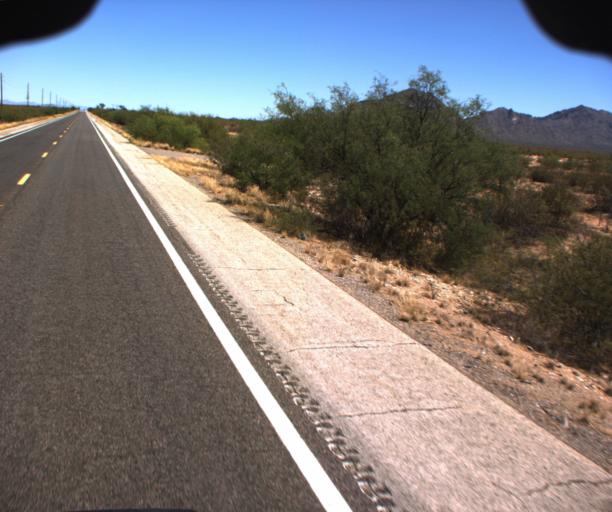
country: US
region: Arizona
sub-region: La Paz County
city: Salome
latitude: 33.8973
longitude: -113.3148
